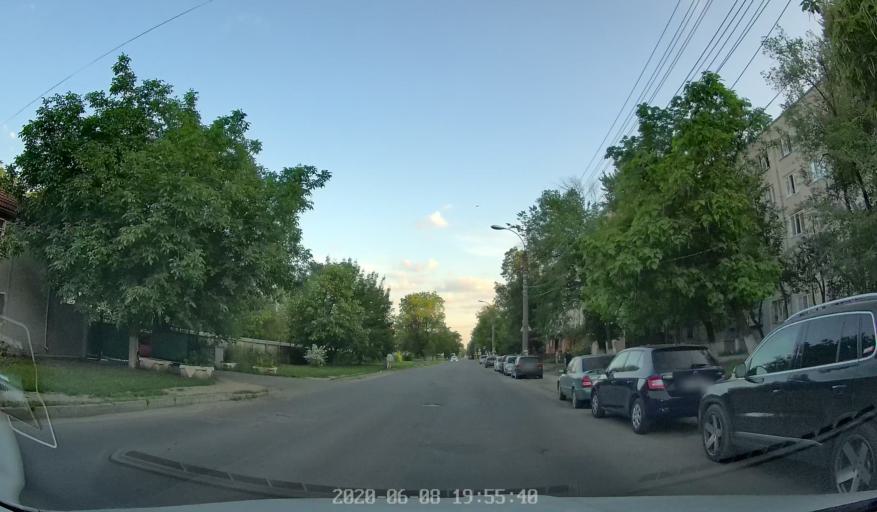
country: MD
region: Chisinau
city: Chisinau
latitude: 47.0273
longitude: 28.8837
